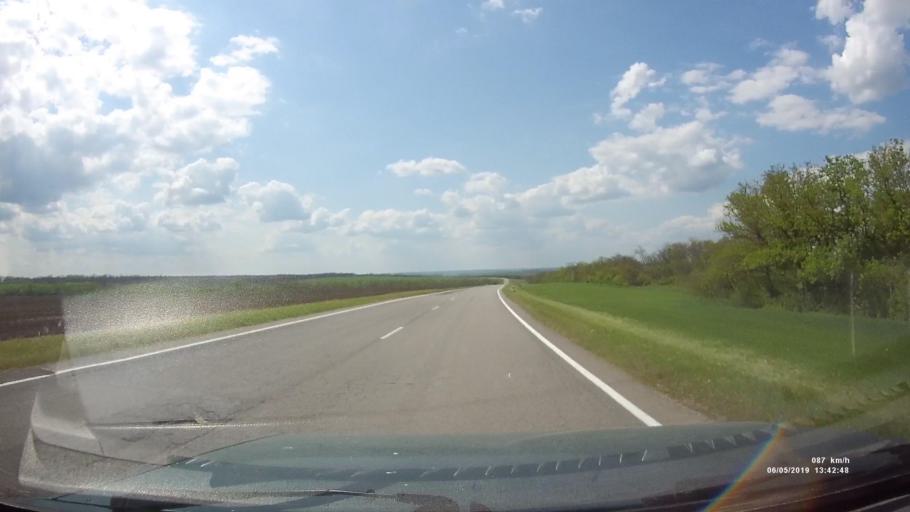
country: RU
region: Rostov
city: Semikarakorsk
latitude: 47.6595
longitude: 40.6502
